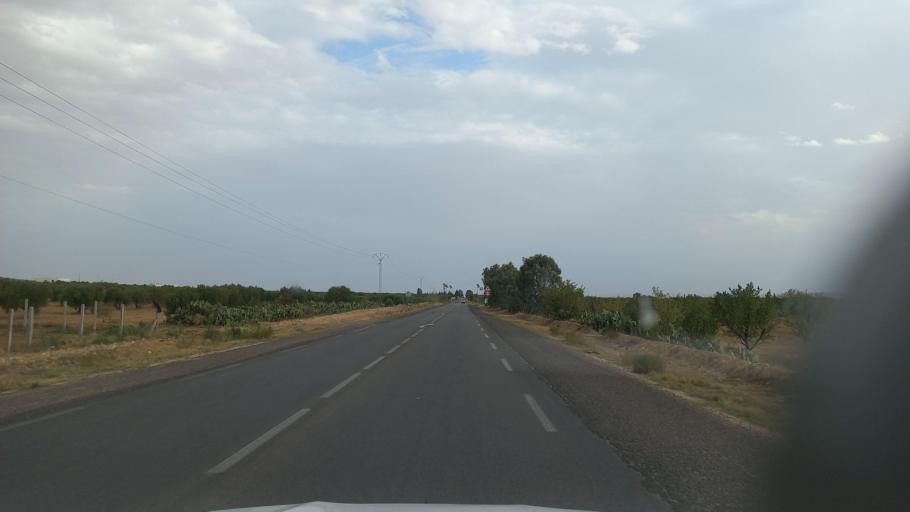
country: TN
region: Al Qasrayn
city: Sbiba
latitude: 35.3111
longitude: 9.0852
